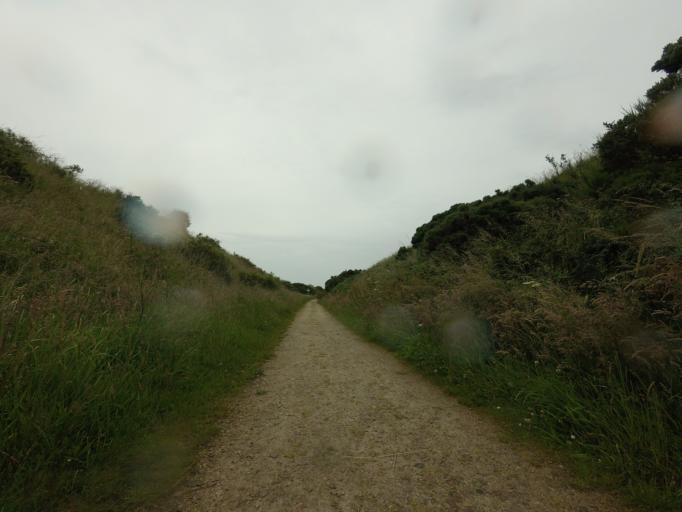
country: GB
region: Scotland
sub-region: Moray
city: Portknockie
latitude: 57.6971
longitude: -2.8499
